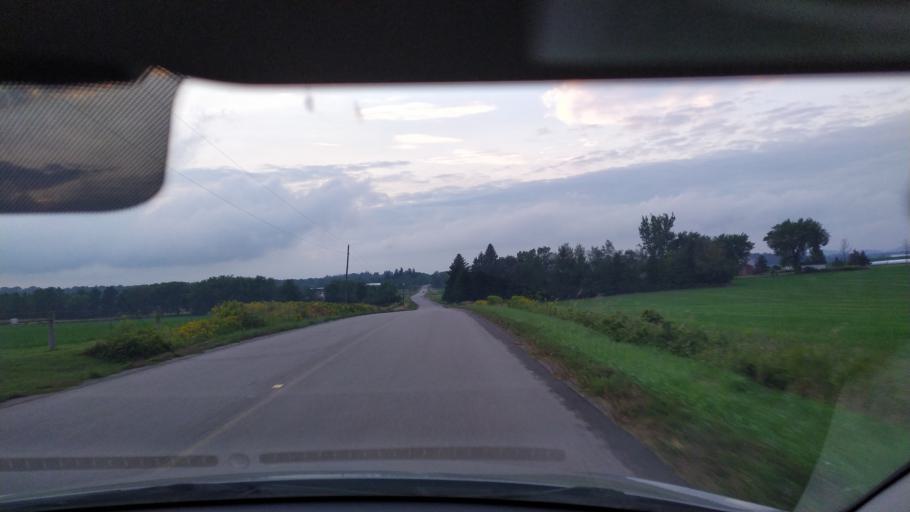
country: CA
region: Ontario
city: Kitchener
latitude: 43.3391
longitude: -80.6305
